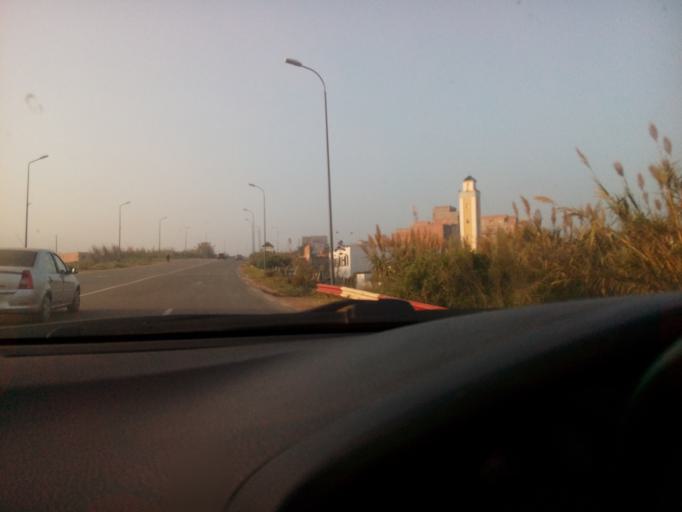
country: DZ
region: Oran
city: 'Ain el Turk
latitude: 35.7276
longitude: -0.8435
